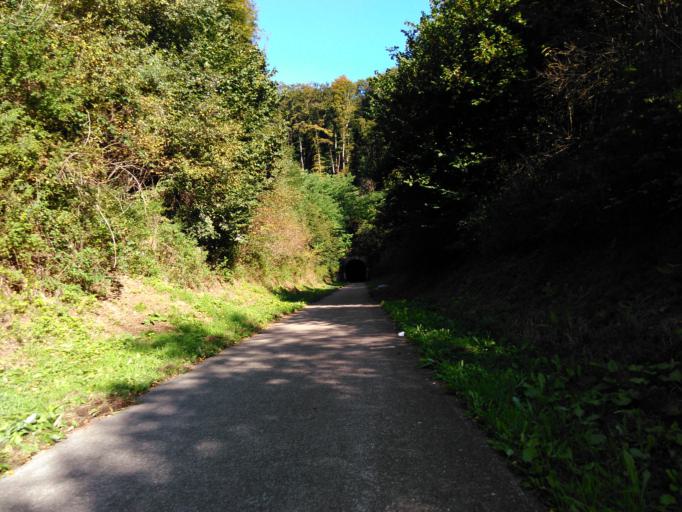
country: LU
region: Luxembourg
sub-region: Canton de Capellen
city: Hobscheid
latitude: 49.6986
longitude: 5.9034
